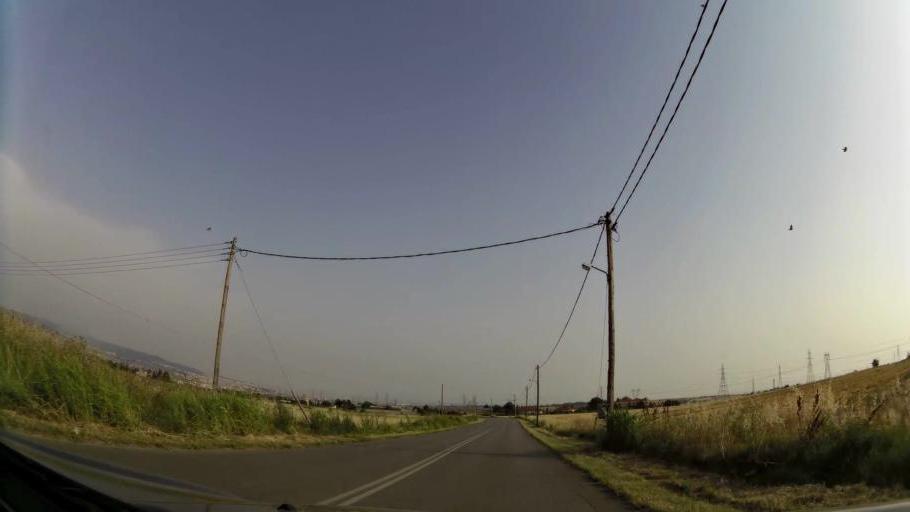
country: GR
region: Central Macedonia
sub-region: Nomos Thessalonikis
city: Oraiokastro
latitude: 40.7129
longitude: 22.9099
